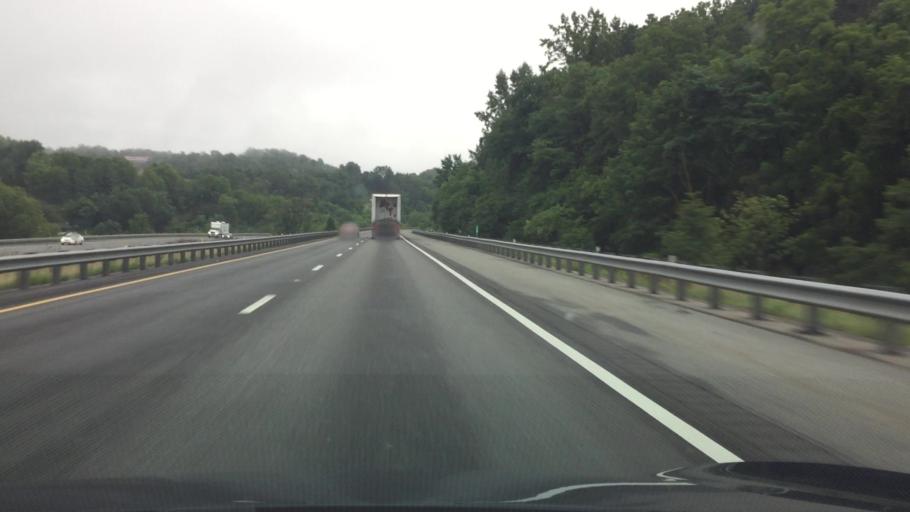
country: US
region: Virginia
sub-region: Montgomery County
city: Shawsville
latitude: 37.1781
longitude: -80.2981
